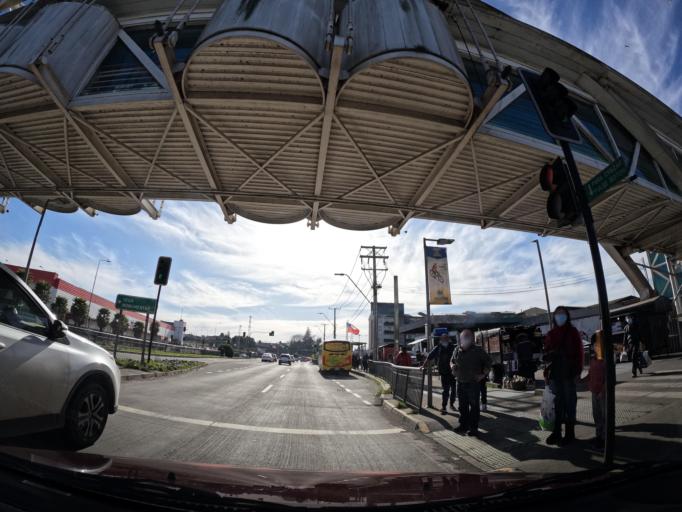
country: CL
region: Biobio
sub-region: Provincia de Concepcion
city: Concepcion
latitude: -36.8084
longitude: -73.0773
